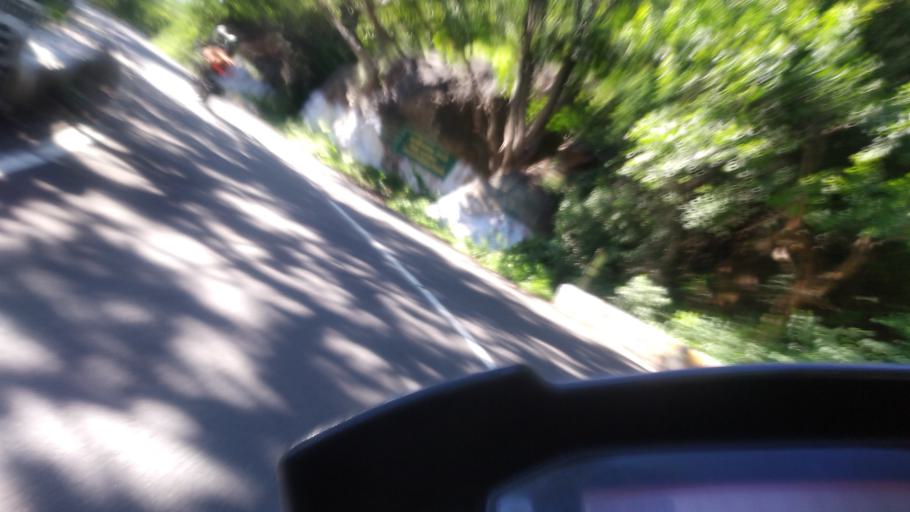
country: IN
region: Tamil Nadu
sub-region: Salem
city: Salem
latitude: 11.7327
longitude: 78.1854
